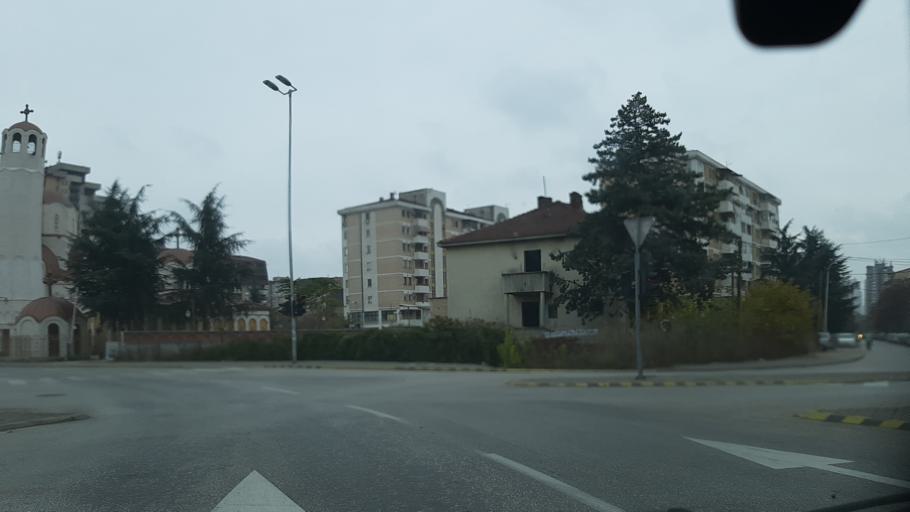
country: MK
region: Karpos
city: Skopje
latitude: 41.9903
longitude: 21.4459
